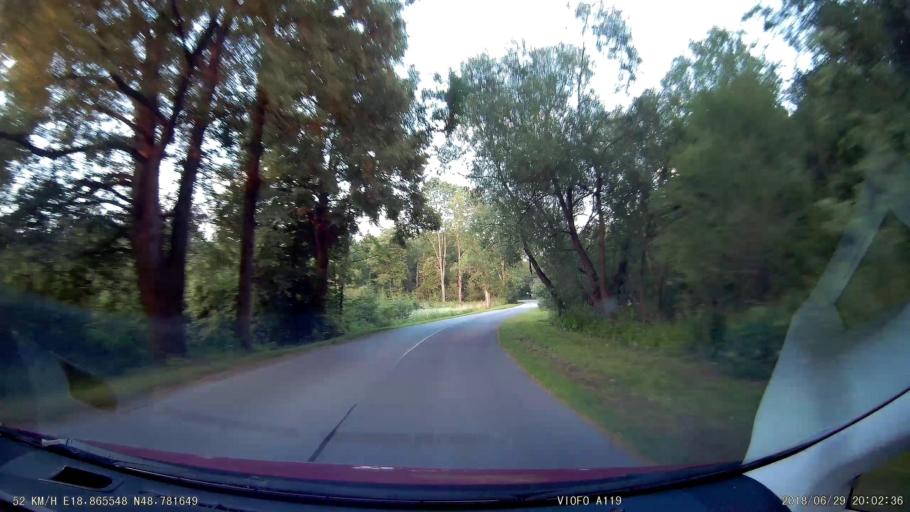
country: SK
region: Banskobystricky
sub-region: Okres Ziar nad Hronom
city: Kremnica
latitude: 48.7817
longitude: 18.8657
